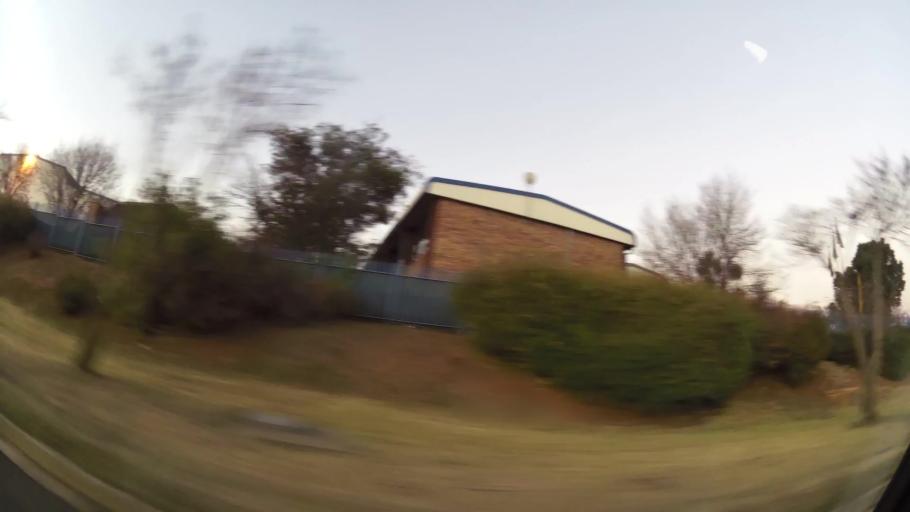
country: ZA
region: Gauteng
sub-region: Ekurhuleni Metropolitan Municipality
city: Germiston
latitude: -26.2679
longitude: 28.1723
